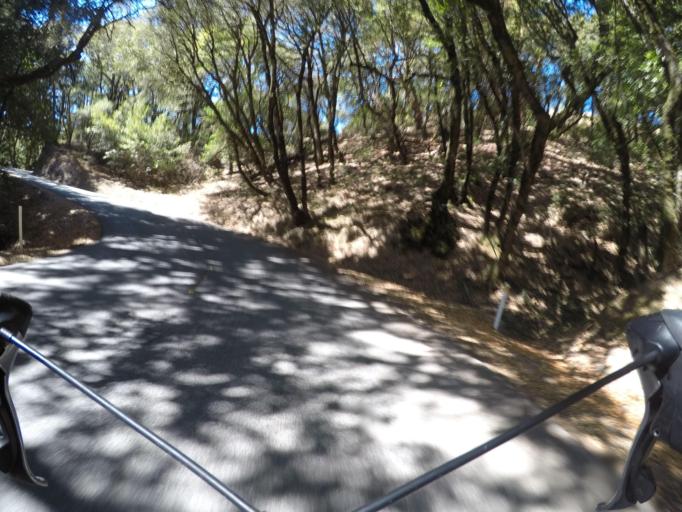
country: US
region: California
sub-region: San Mateo County
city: Portola Valley
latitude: 37.3165
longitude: -122.1935
